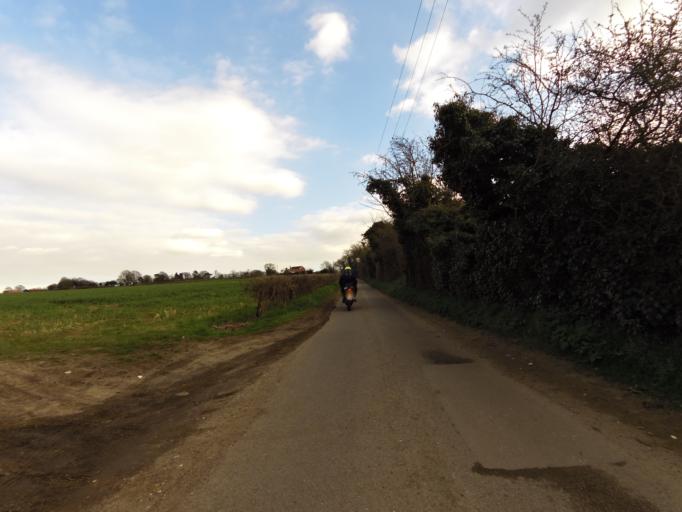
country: GB
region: England
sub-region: Suffolk
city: Ipswich
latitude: 52.0914
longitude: 1.1404
